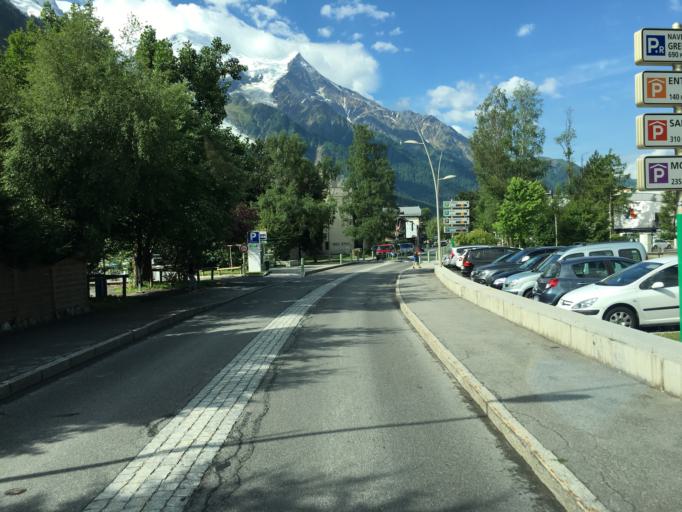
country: FR
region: Rhone-Alpes
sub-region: Departement de la Haute-Savoie
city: Chamonix-Mont-Blanc
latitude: 45.9264
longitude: 6.8748
